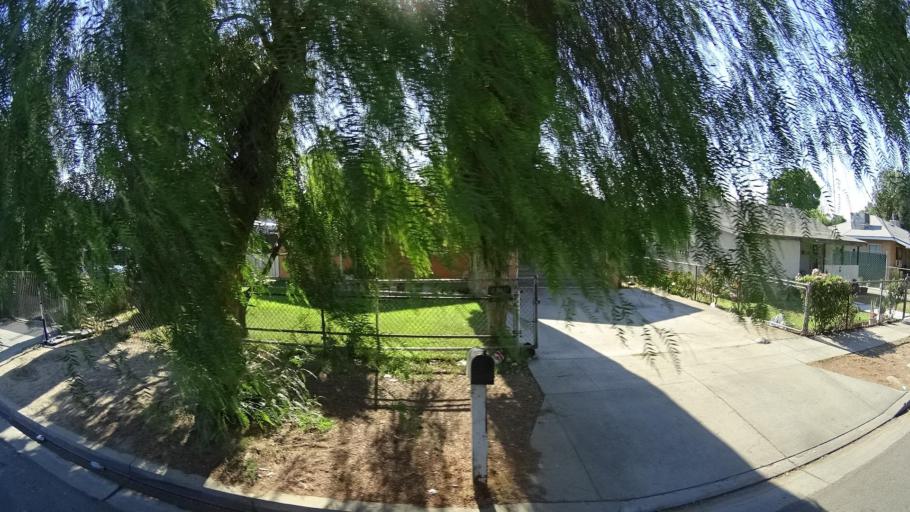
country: US
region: California
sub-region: Fresno County
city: Fresno
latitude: 36.7130
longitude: -119.7446
